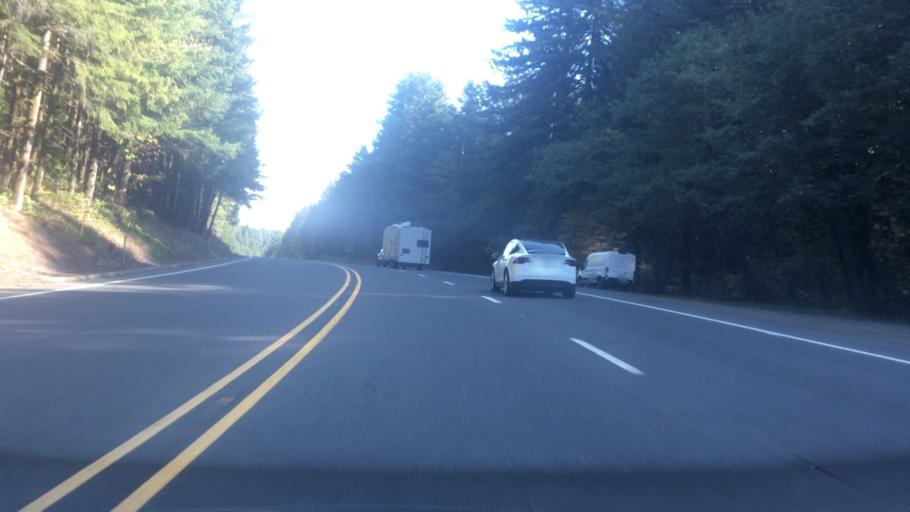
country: US
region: Oregon
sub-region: Polk County
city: Grand Ronde
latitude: 45.0605
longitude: -123.6990
